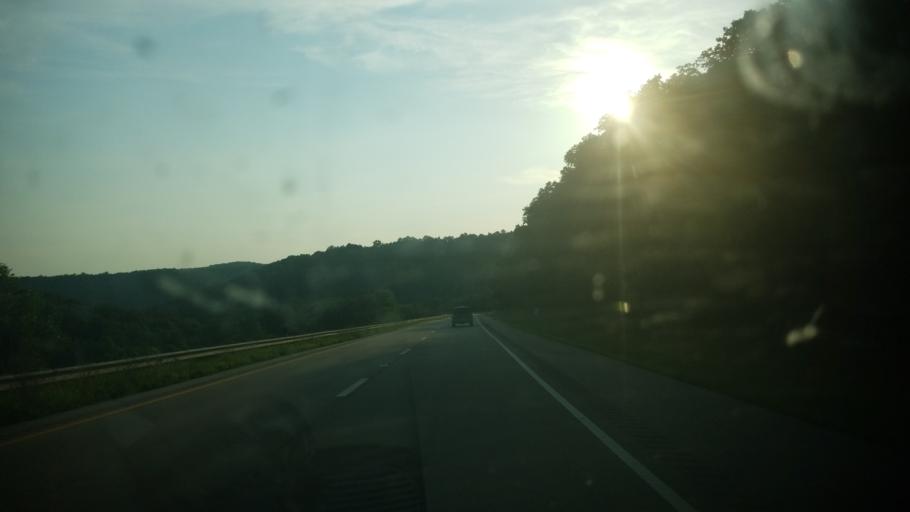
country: US
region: Ohio
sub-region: Adams County
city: Peebles
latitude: 39.0194
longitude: -83.2826
